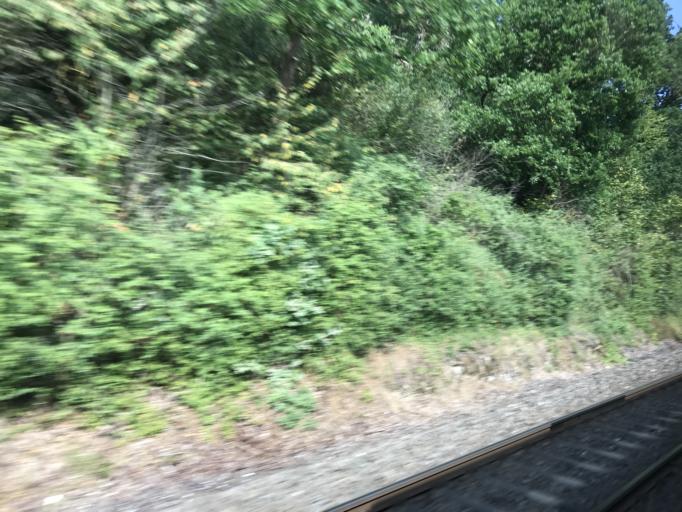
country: DE
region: Hesse
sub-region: Regierungsbezirk Giessen
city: Runkel
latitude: 50.3732
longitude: 8.1337
